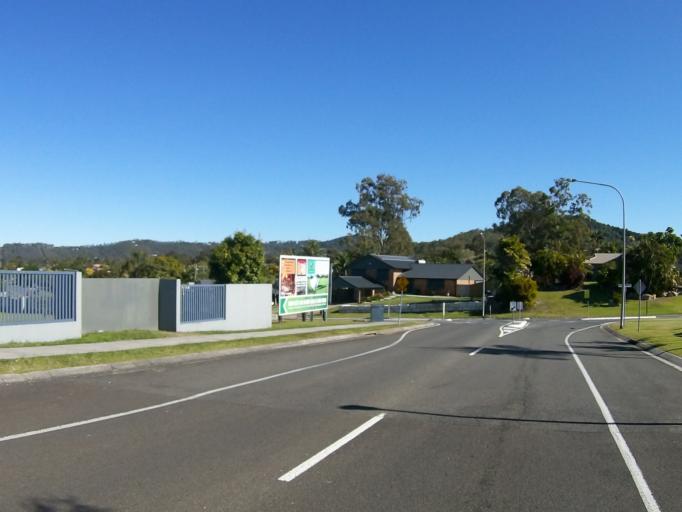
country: AU
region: Queensland
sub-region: Logan
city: Windaroo
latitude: -27.7420
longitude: 153.1931
